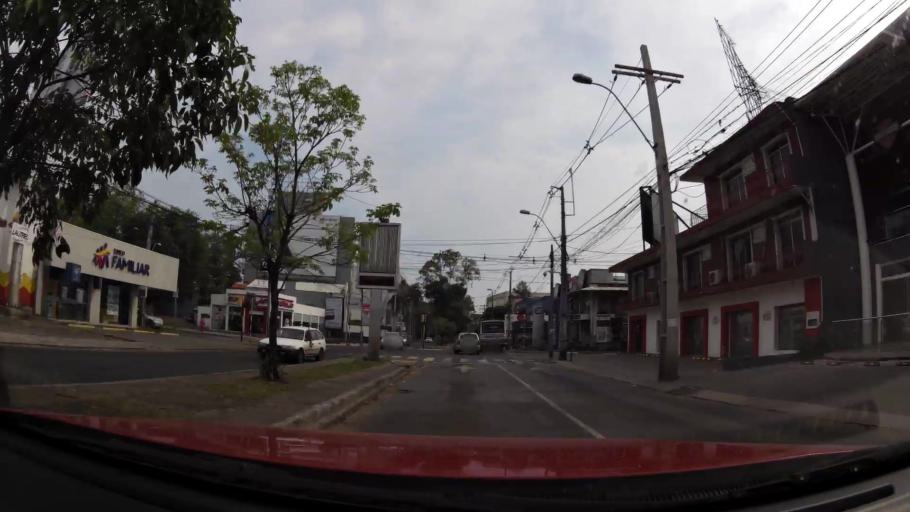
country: PY
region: Asuncion
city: Asuncion
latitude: -25.2894
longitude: -57.5736
